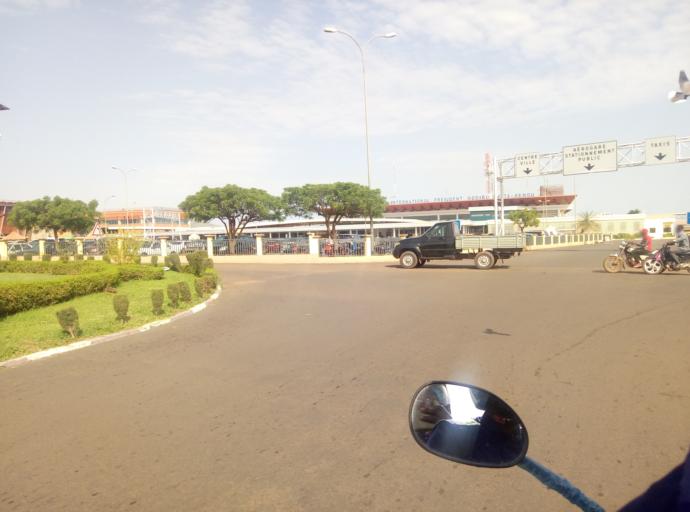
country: ML
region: Bamako
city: Bamako
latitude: 12.5416
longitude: -7.9486
